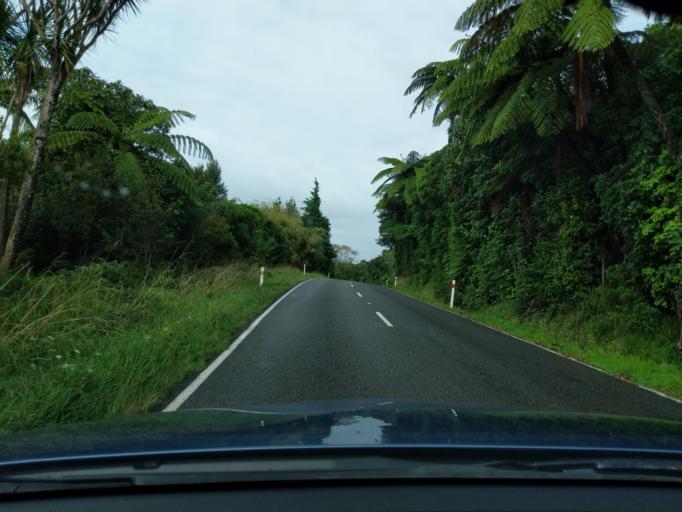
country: NZ
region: Tasman
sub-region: Tasman District
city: Takaka
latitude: -40.6457
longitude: 172.6593
